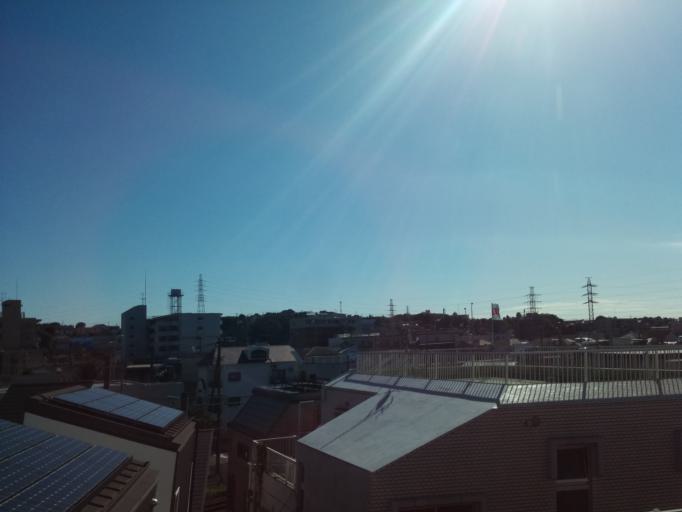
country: JP
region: Kanagawa
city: Yokohama
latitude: 35.5182
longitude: 139.6300
